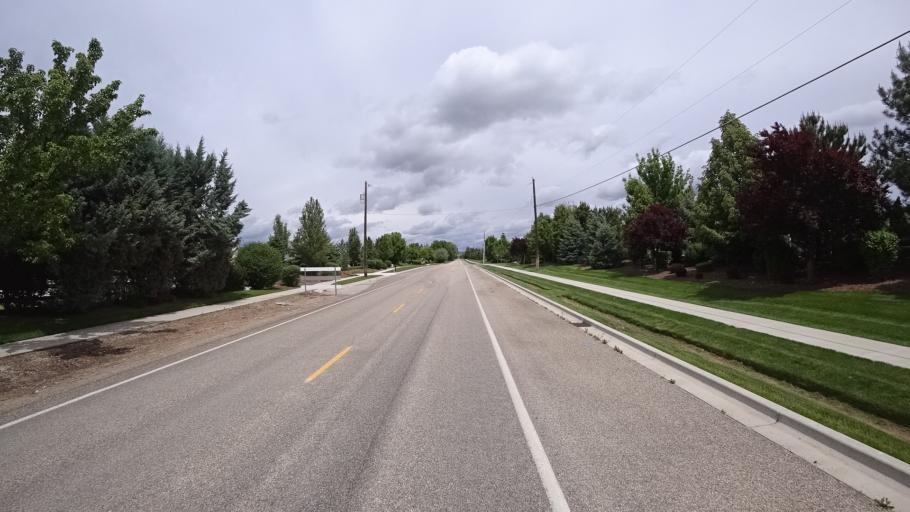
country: US
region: Idaho
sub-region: Ada County
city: Eagle
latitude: 43.7114
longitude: -116.4035
